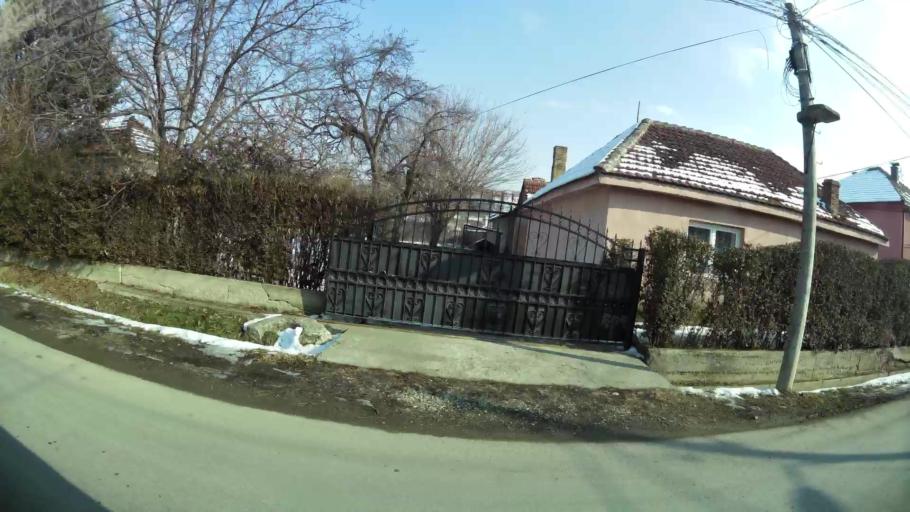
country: MK
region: Suto Orizari
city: Suto Orizare
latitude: 42.0263
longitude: 21.3751
